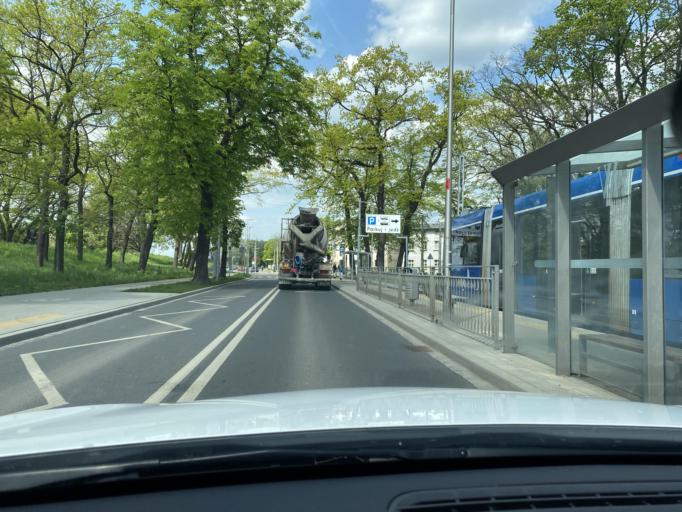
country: PL
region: Lower Silesian Voivodeship
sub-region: Powiat wroclawski
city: Wroclaw
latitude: 51.1374
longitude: 16.9941
